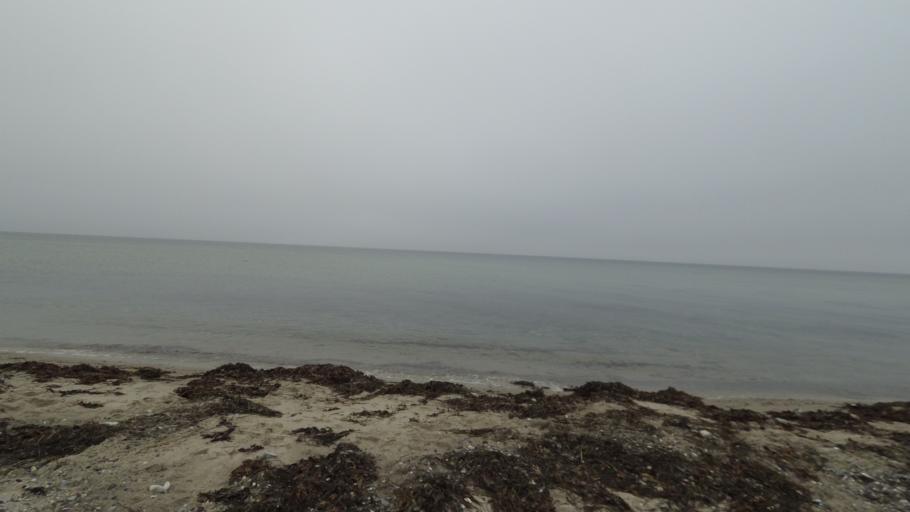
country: DK
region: Central Jutland
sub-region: Arhus Kommune
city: Malling
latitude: 55.9563
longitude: 10.2652
